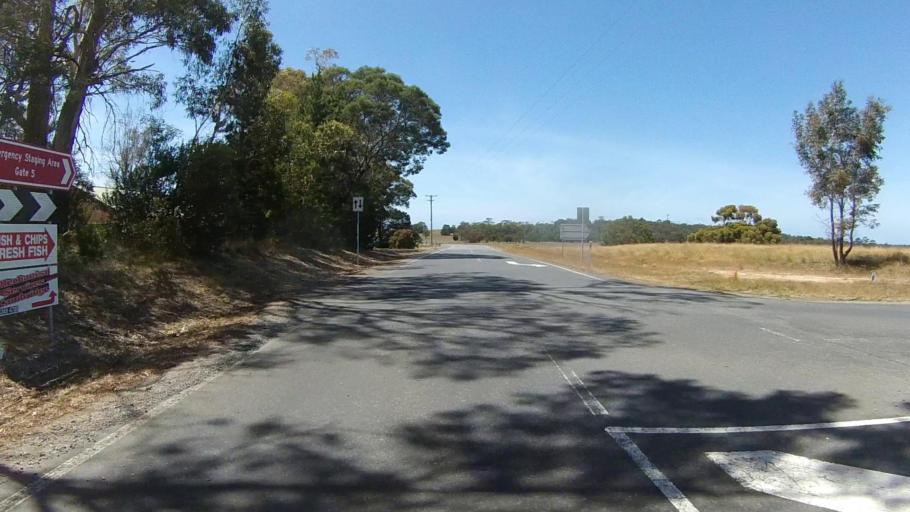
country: AU
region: Tasmania
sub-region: Clarence
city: Seven Mile Beach
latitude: -42.8311
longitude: 147.4951
